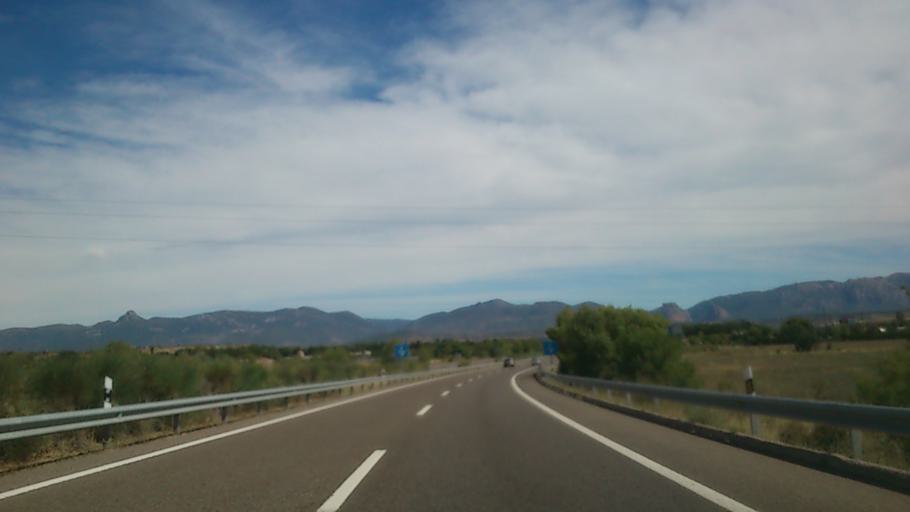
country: ES
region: Aragon
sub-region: Provincia de Huesca
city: Huesca
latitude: 42.1412
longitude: -0.4312
